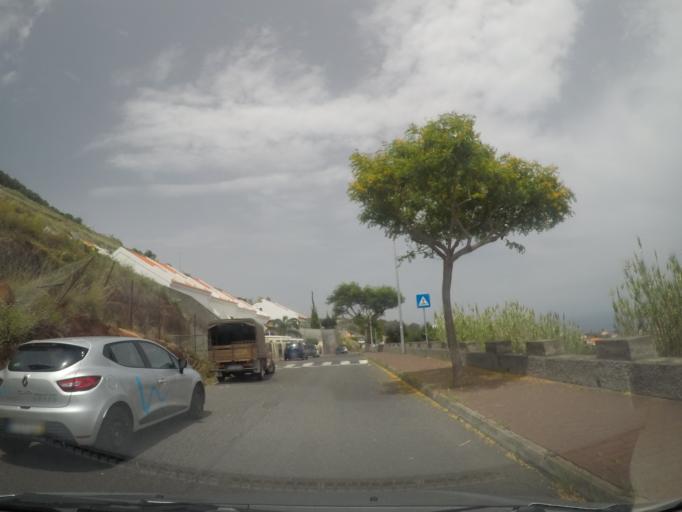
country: PT
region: Madeira
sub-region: Santa Cruz
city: Camacha
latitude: 32.6565
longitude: -16.8328
